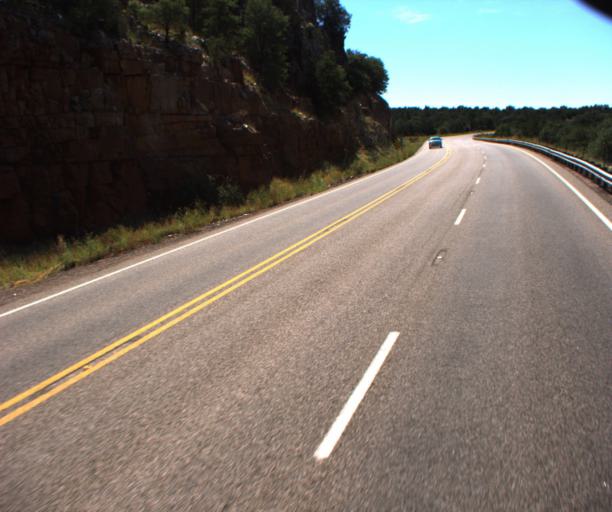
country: US
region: Arizona
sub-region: Navajo County
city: Cibecue
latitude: 33.7350
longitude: -110.5265
